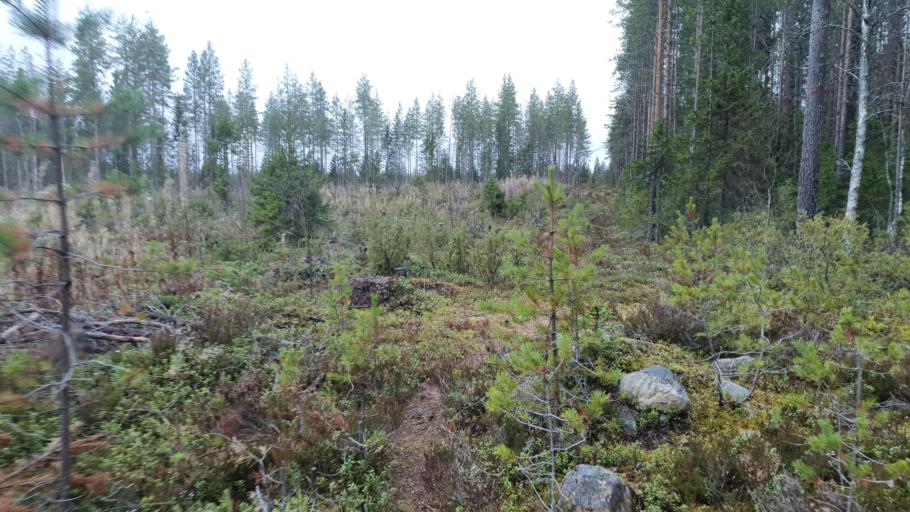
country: FI
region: Kainuu
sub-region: Kehys-Kainuu
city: Kuhmo
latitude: 64.1330
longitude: 29.3903
